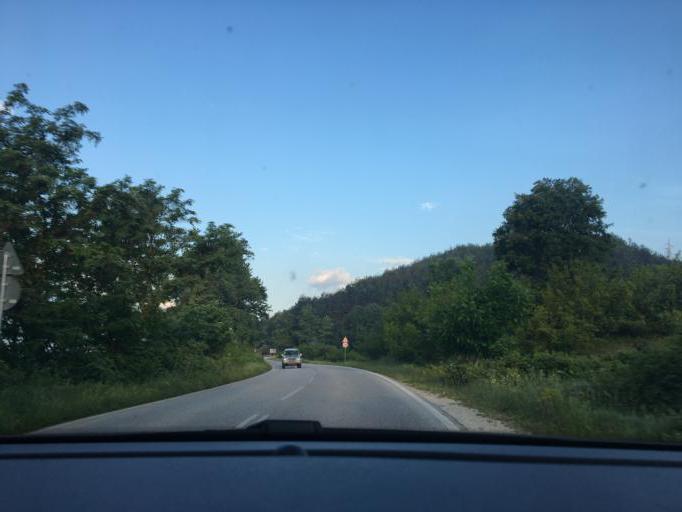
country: BG
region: Blagoevgrad
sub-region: Obshtina Petrich
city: Petrich
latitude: 41.3970
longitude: 23.0554
